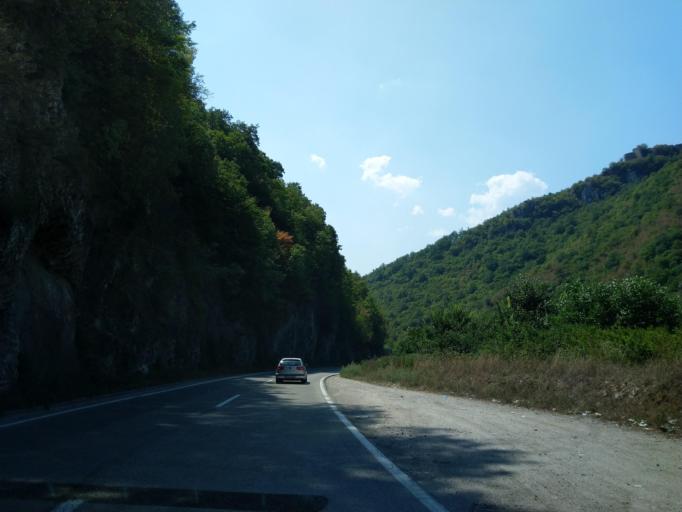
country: RS
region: Central Serbia
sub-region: Zlatiborski Okrug
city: Prijepolje
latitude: 43.4570
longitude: 19.6446
